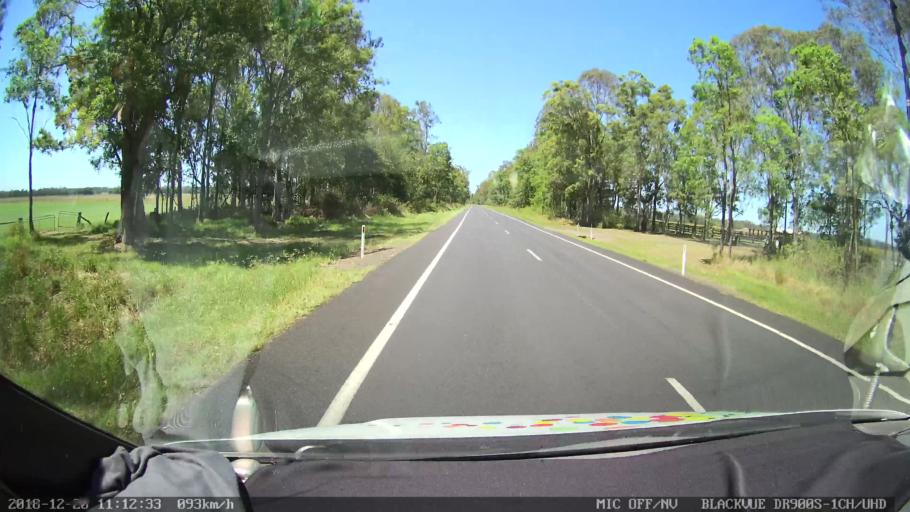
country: AU
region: New South Wales
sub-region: Richmond Valley
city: Casino
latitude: -28.9756
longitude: 153.0106
